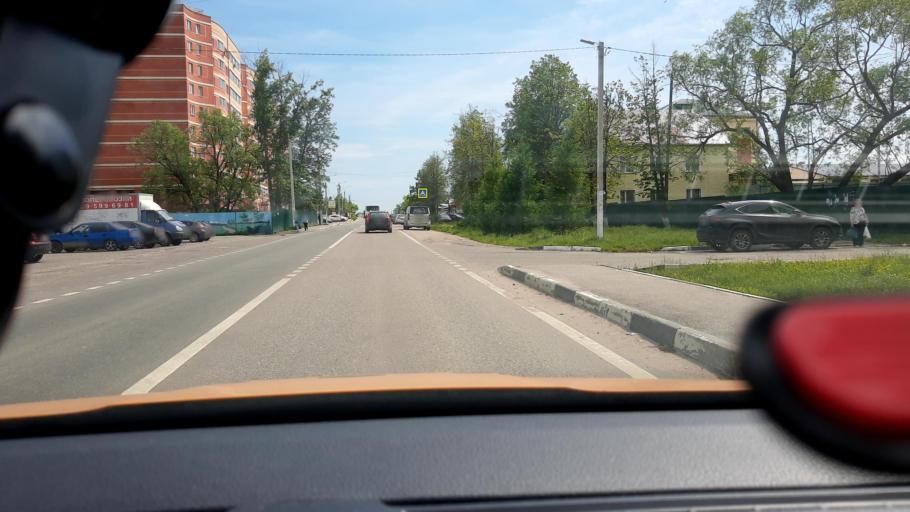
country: RU
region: Moskovskaya
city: Kubinka
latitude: 55.5760
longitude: 36.6947
